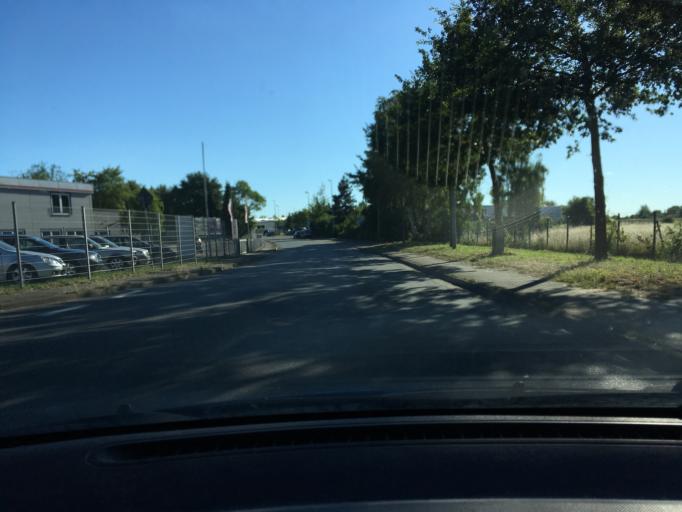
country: DE
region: Lower Saxony
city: Wendisch Evern
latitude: 53.2493
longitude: 10.4693
